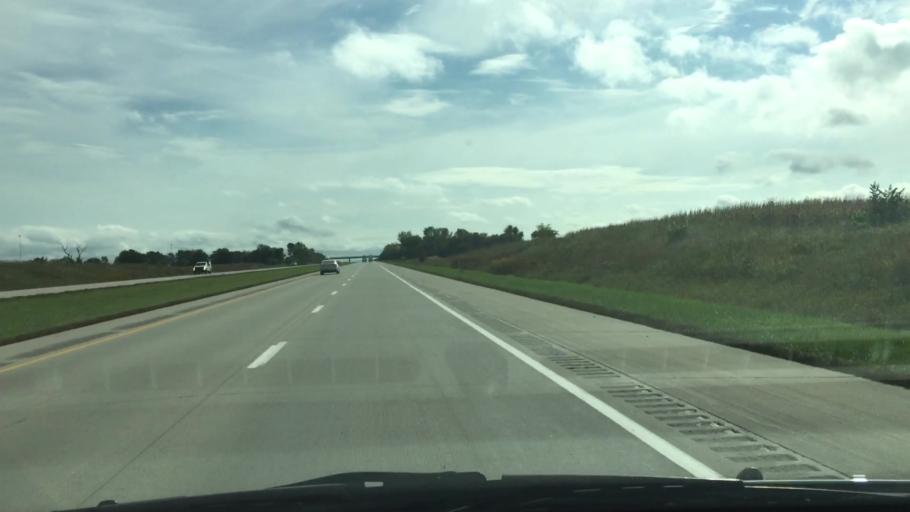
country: US
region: Iowa
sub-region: Clarke County
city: Osceola
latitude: 40.9516
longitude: -93.7994
